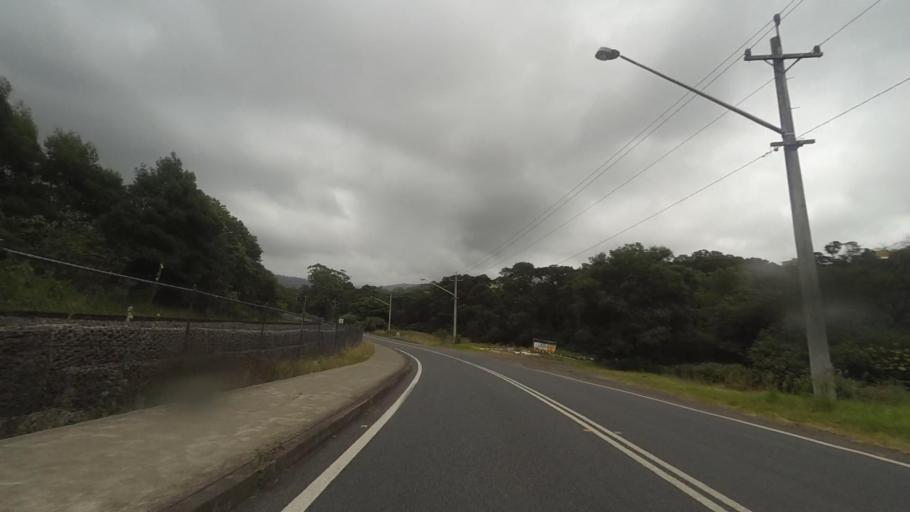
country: AU
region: New South Wales
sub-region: Wollongong
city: Cordeaux Heights
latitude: -34.4416
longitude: 150.8416
